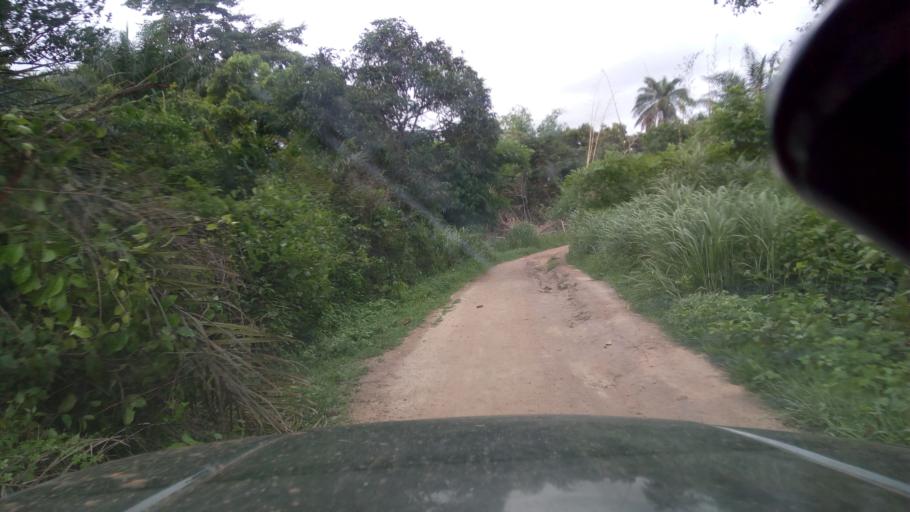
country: SL
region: Northern Province
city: Rokupr
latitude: 8.6303
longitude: -12.4542
